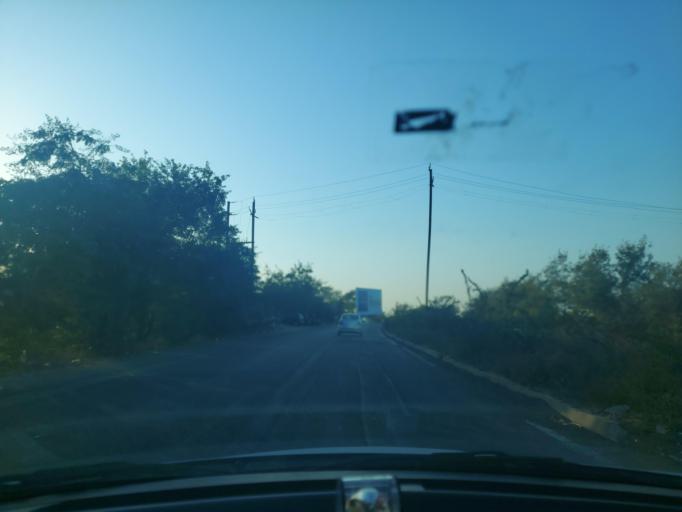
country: IN
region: Madhya Pradesh
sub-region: Ujjain
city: Ujjain
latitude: 23.0981
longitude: 75.8123
